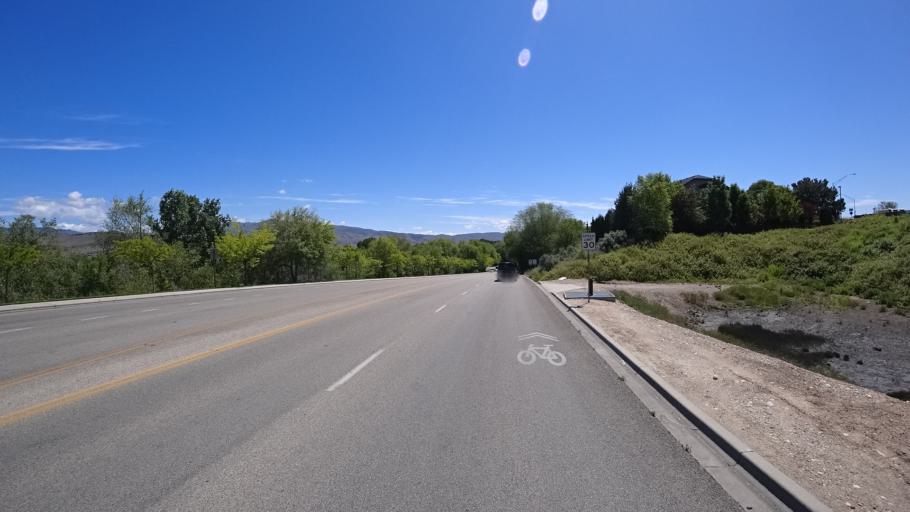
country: US
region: Idaho
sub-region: Ada County
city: Boise
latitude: 43.5683
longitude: -116.1816
